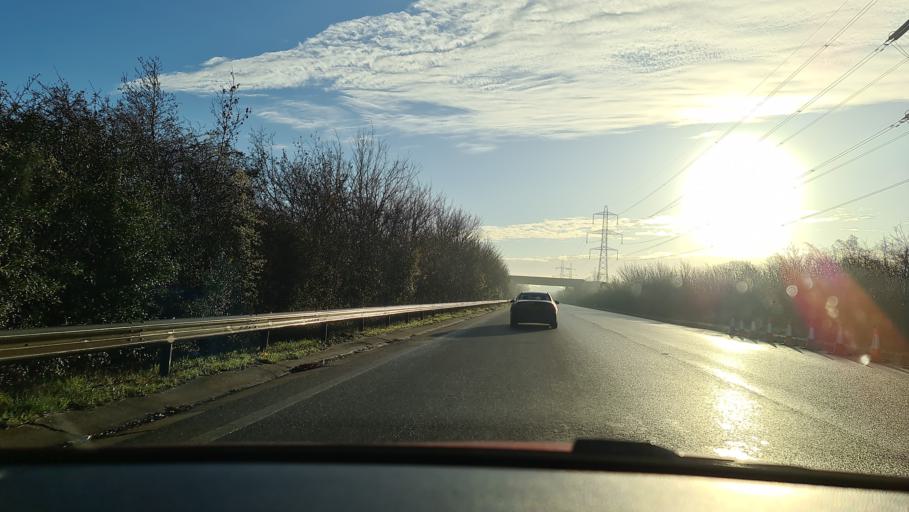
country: GB
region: England
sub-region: Buckinghamshire
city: Wendover
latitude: 51.7662
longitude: -0.7570
